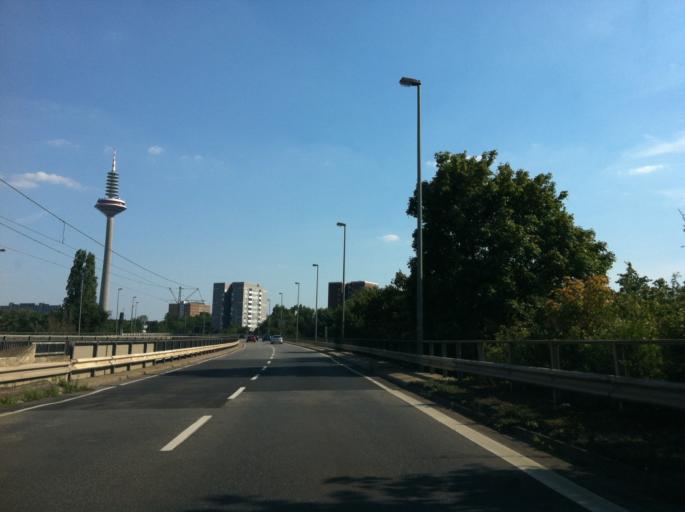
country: DE
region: Hesse
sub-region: Regierungsbezirk Darmstadt
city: Frankfurt am Main
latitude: 50.1435
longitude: 8.6422
